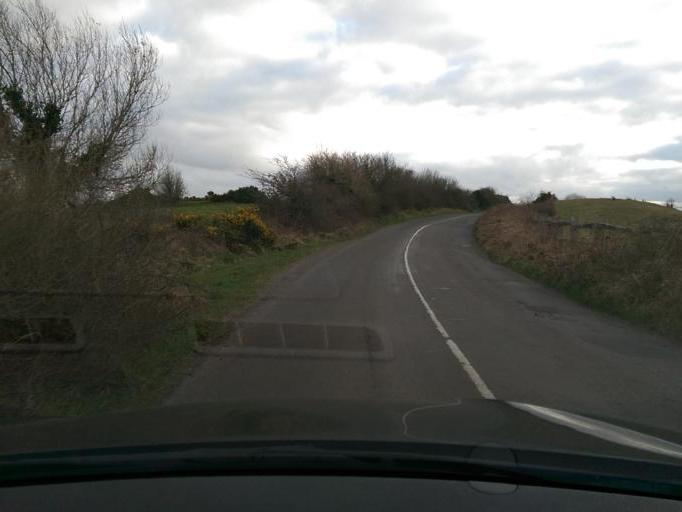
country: IE
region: Leinster
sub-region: Uibh Fhaili
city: Banagher
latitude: 53.2940
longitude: -8.0144
